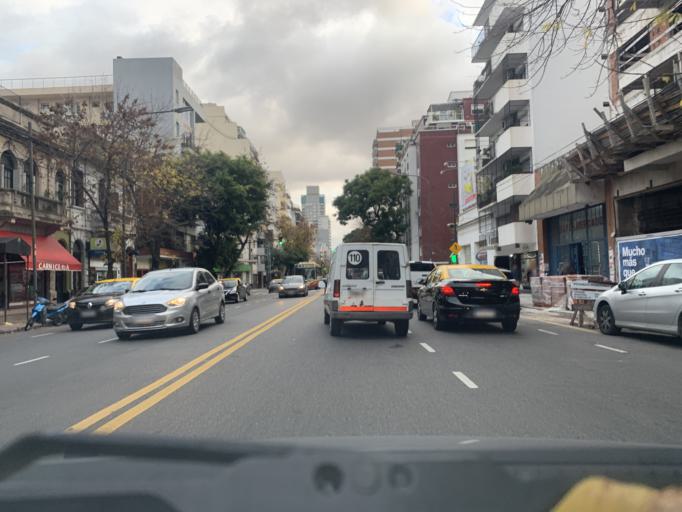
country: AR
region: Buenos Aires F.D.
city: Colegiales
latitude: -34.5784
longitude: -58.4497
